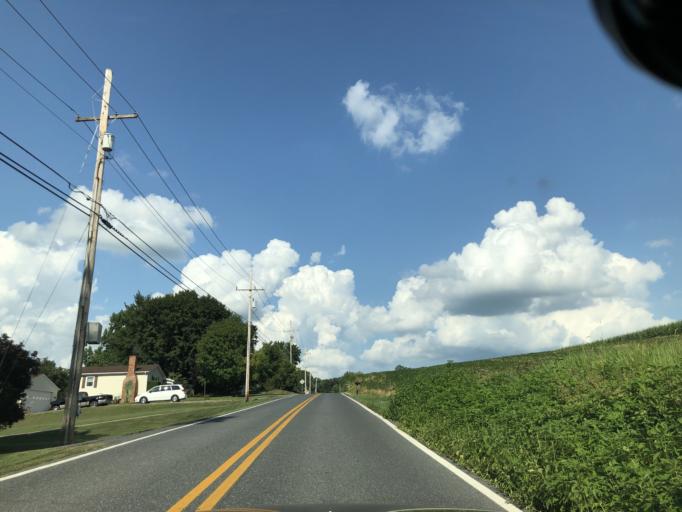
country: US
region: Maryland
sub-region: Frederick County
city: Linganore
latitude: 39.4698
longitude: -77.1662
